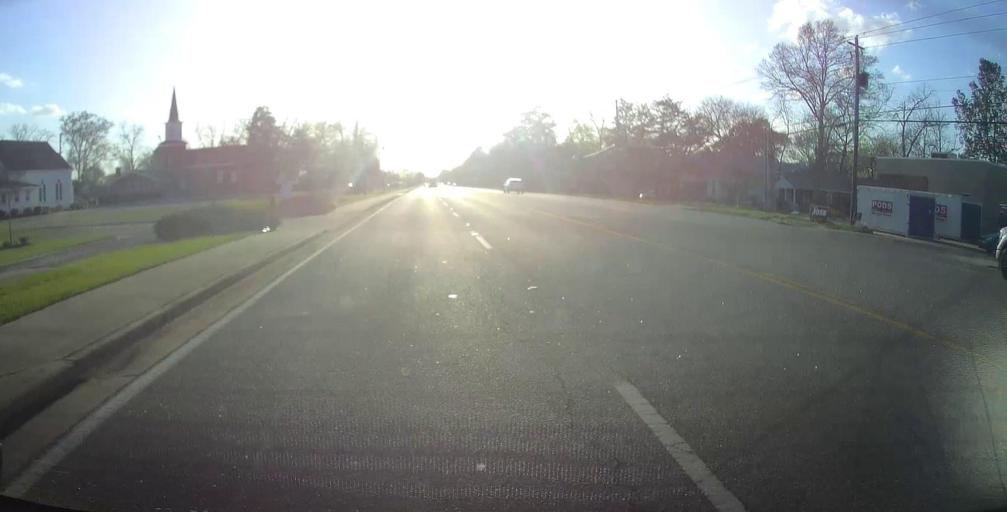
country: US
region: Georgia
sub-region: Evans County
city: Claxton
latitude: 32.1587
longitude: -81.9336
